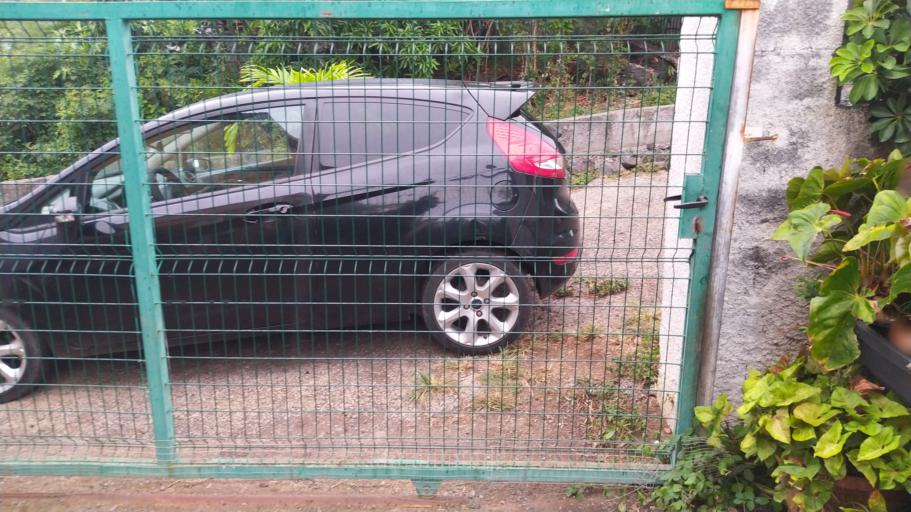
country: RE
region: Reunion
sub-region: Reunion
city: Saint-Pierre
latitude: -21.2979
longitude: 55.4624
